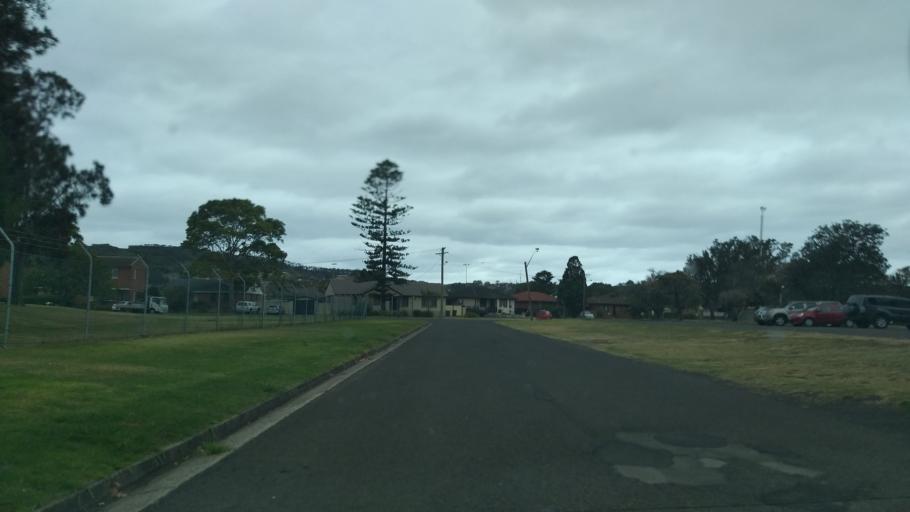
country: AU
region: New South Wales
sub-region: Wollongong
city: Berkeley
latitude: -34.4819
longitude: 150.8479
